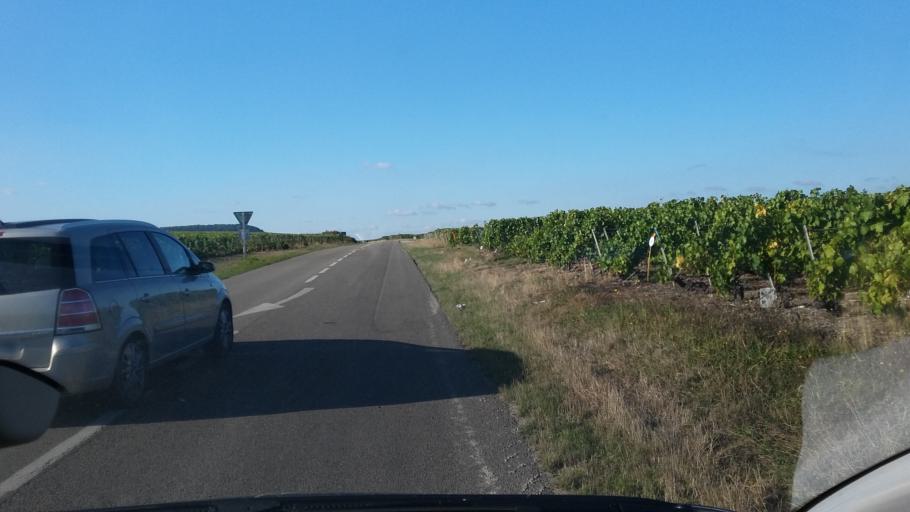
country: FR
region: Champagne-Ardenne
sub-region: Departement de la Marne
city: Le Mesnil-sur-Oger
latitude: 48.9440
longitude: 4.0296
